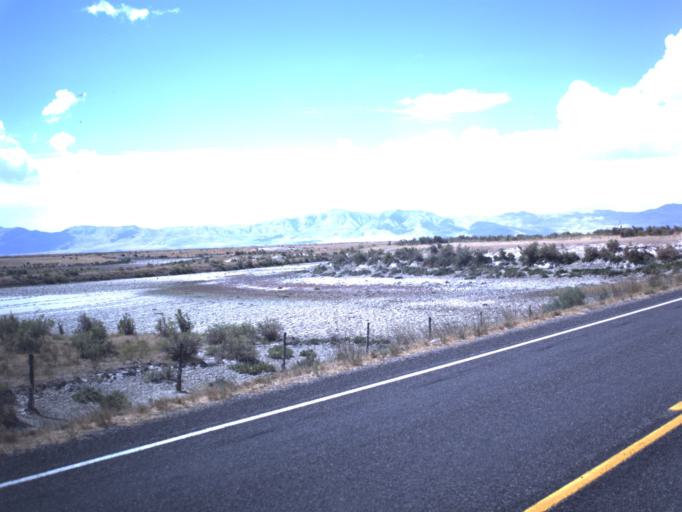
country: US
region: Utah
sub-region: Box Elder County
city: Elwood
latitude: 41.5761
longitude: -112.2312
